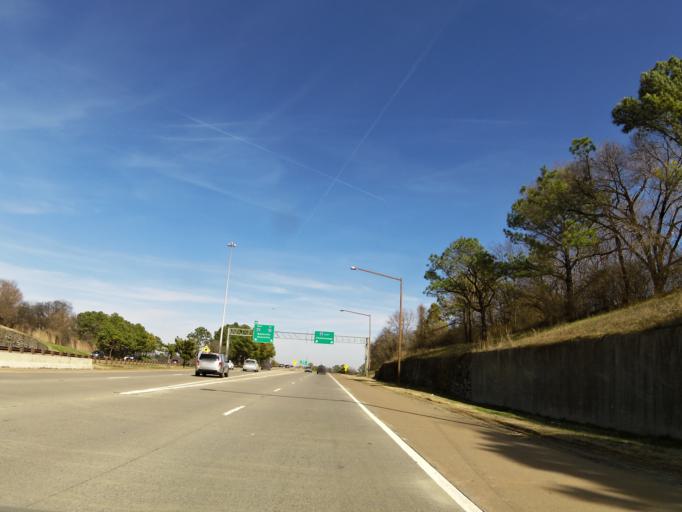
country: US
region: Tennessee
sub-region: Davidson County
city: Oak Hill
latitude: 36.1250
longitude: -86.7337
